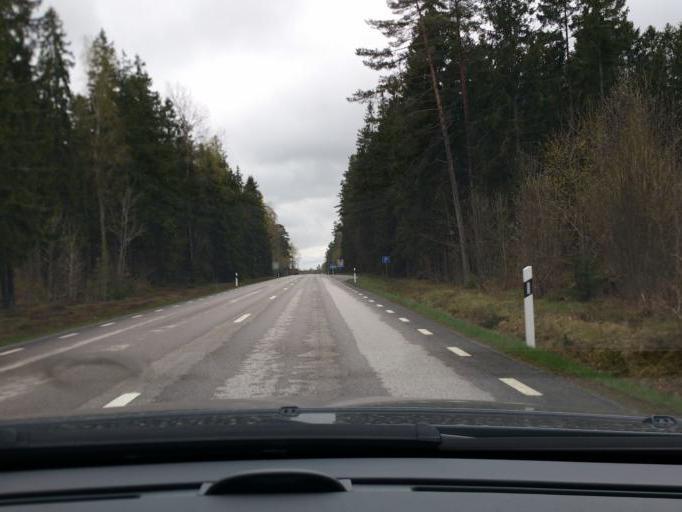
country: SE
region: Kronoberg
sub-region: Vaxjo Kommun
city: Vaexjoe
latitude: 56.9472
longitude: 14.7219
